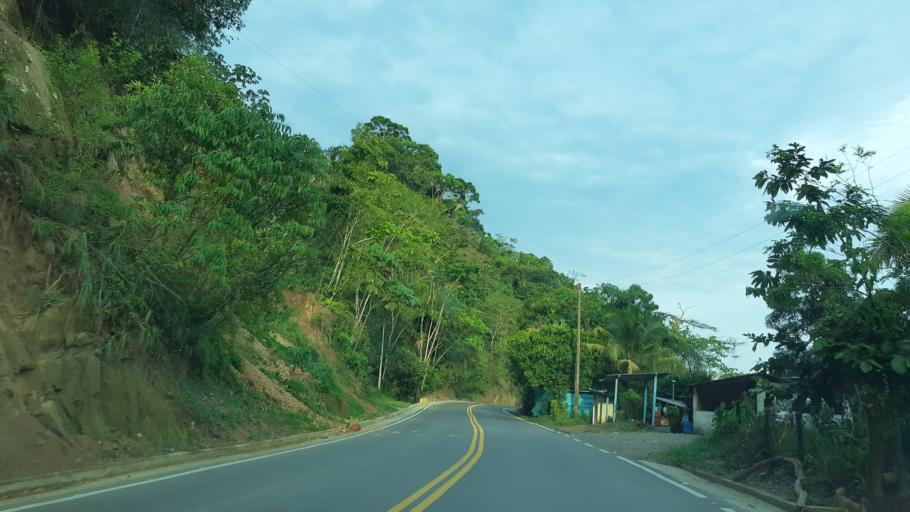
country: CO
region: Boyaca
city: San Luis de Gaceno
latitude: 4.8303
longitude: -73.1162
